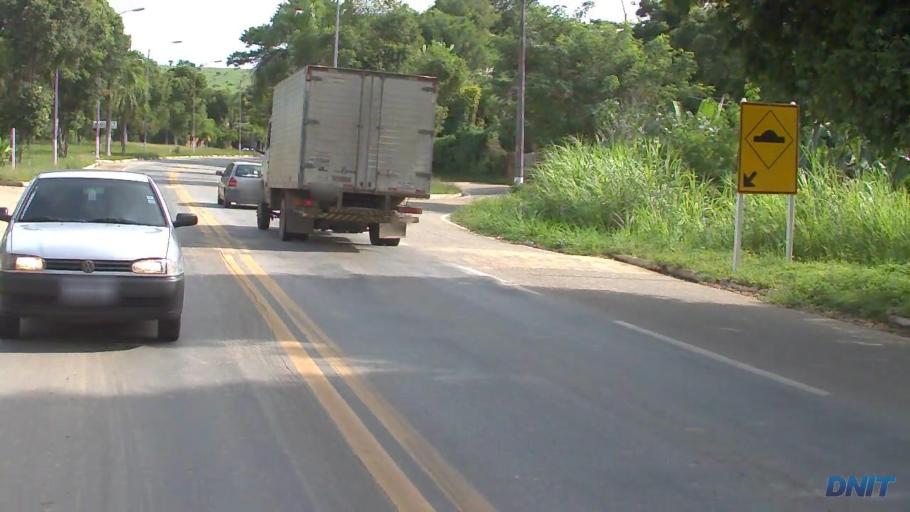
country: BR
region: Minas Gerais
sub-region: Belo Oriente
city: Belo Oriente
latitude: -19.2322
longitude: -42.3284
